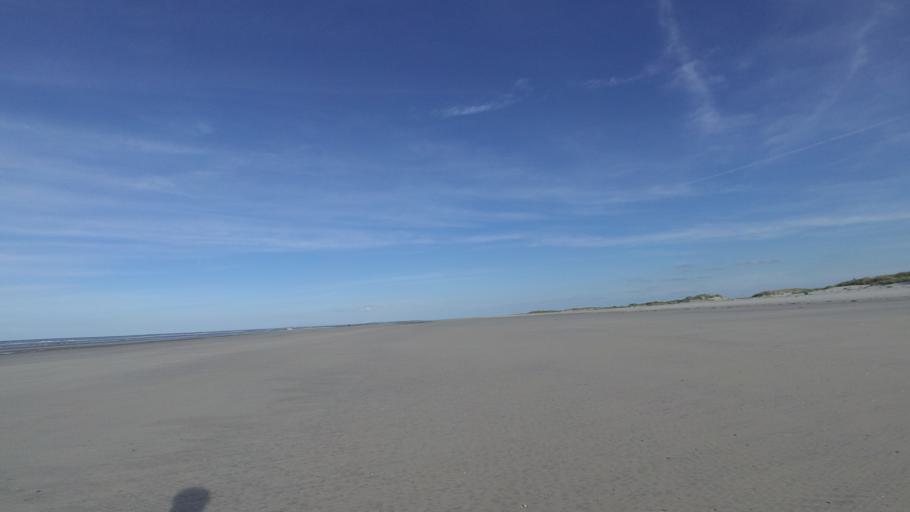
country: NL
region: Friesland
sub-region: Gemeente Dongeradeel
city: Ternaard
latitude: 53.4680
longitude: 5.9211
